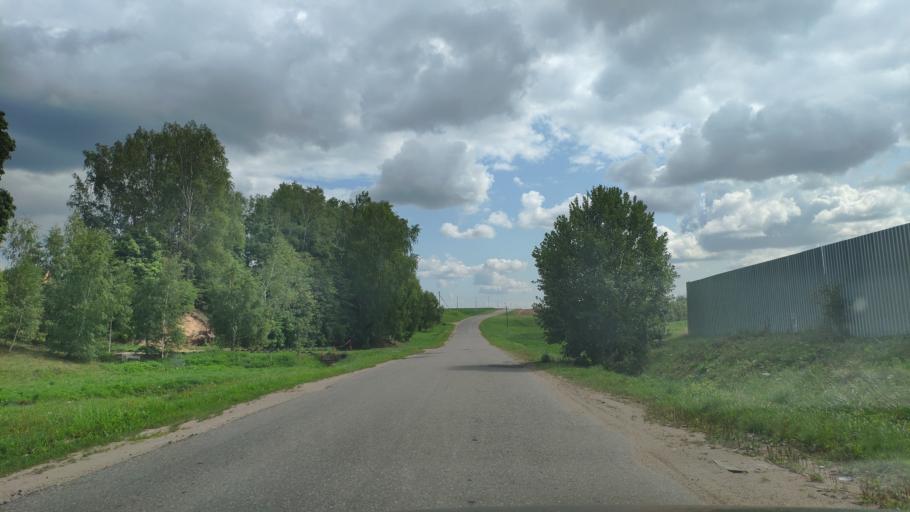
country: BY
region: Minsk
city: Khatsyezhyna
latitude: 53.8530
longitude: 27.3086
